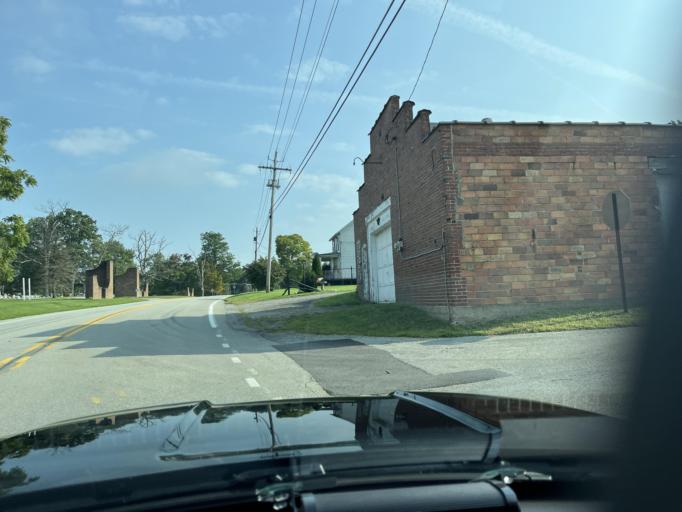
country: US
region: Pennsylvania
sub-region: Fayette County
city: Hopwood
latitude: 39.8552
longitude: -79.7134
